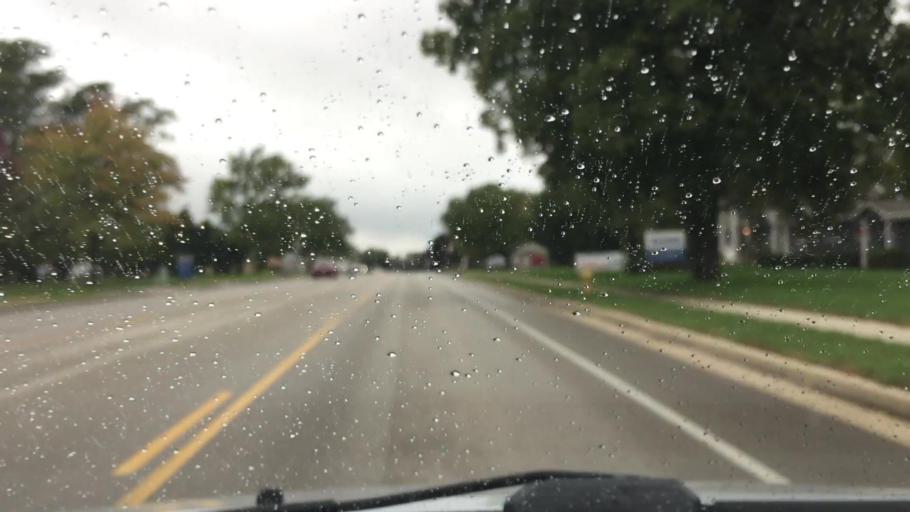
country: US
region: Wisconsin
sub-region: Waukesha County
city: Oconomowoc
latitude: 43.0993
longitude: -88.4838
